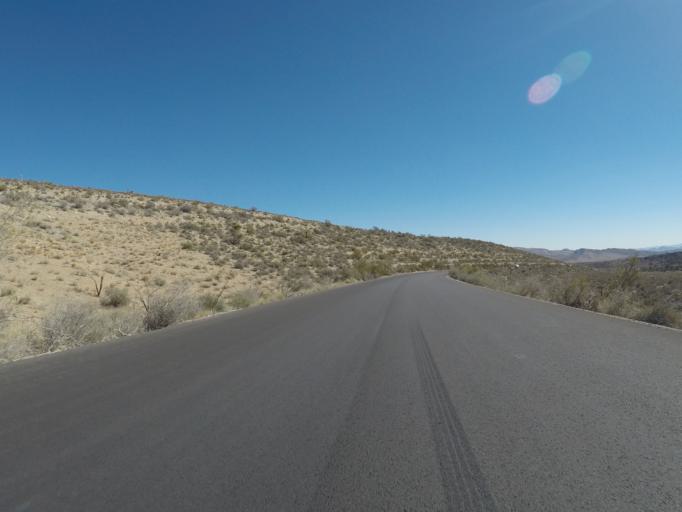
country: US
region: Nevada
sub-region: Clark County
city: Summerlin South
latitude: 36.1548
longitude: -115.4888
